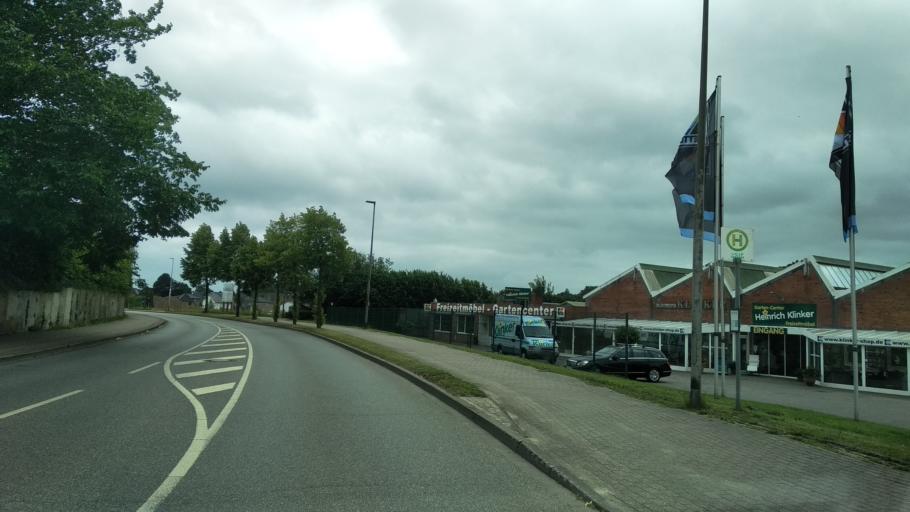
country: DE
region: Schleswig-Holstein
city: Schleswig
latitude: 54.5329
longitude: 9.5566
